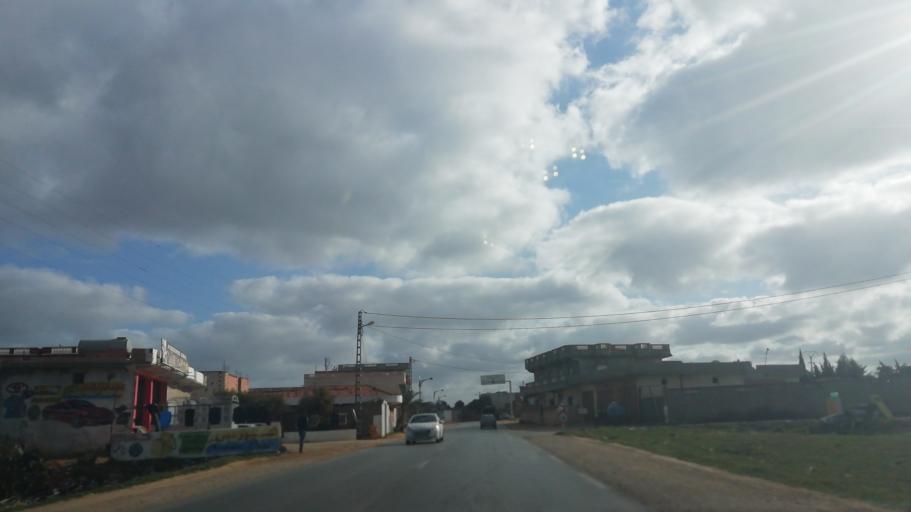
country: DZ
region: Relizane
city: Mazouna
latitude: 36.2609
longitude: 0.6112
